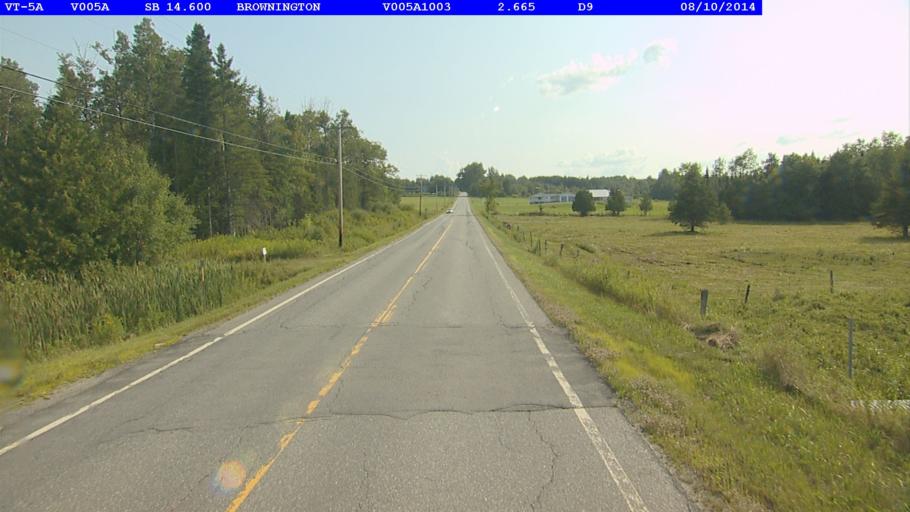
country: US
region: Vermont
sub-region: Orleans County
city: Newport
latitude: 44.8208
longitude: -72.0733
